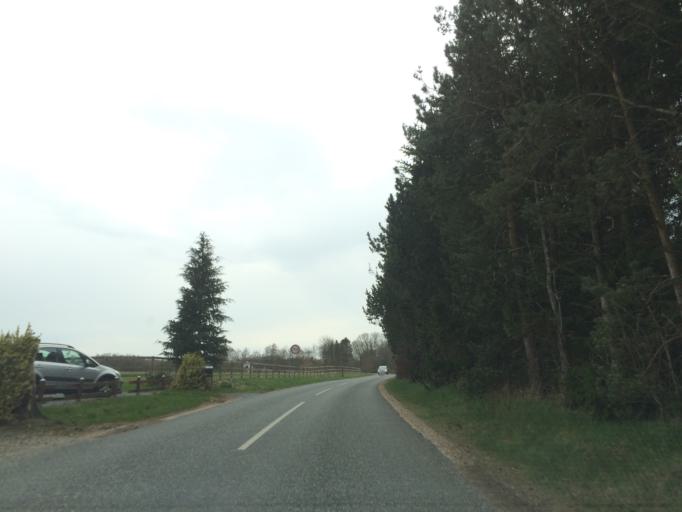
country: DK
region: Central Jutland
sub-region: Viborg Kommune
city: Bjerringbro
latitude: 56.2788
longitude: 9.6728
